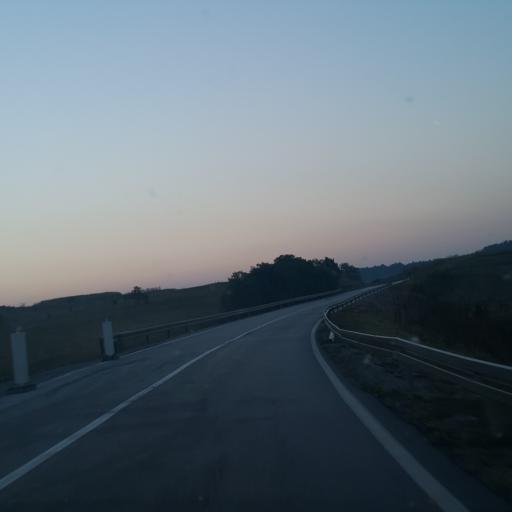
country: RS
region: Central Serbia
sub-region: Nisavski Okrug
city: Svrljig
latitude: 43.4542
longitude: 22.1871
